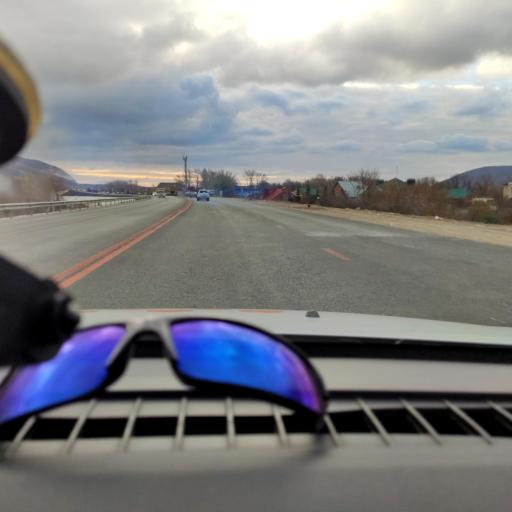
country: RU
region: Samara
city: Volzhskiy
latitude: 53.4196
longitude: 50.1278
